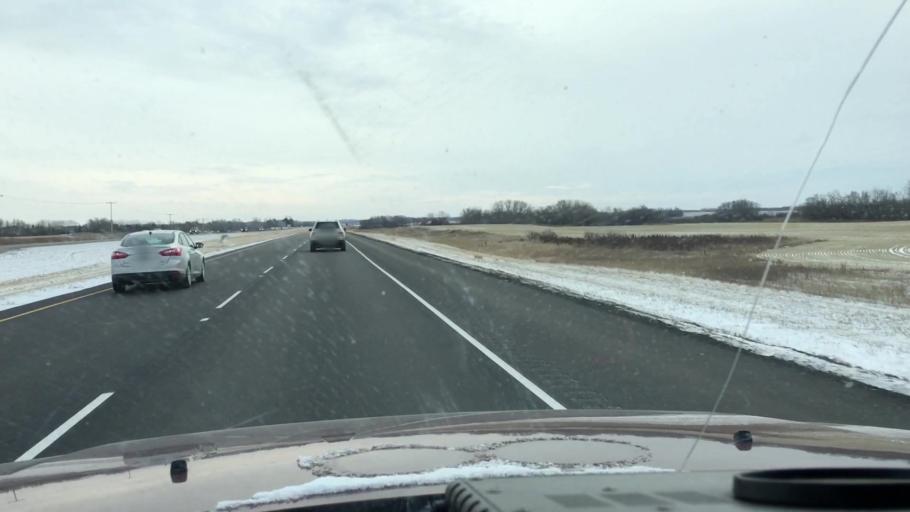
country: CA
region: Saskatchewan
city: Saskatoon
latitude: 52.0259
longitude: -106.5813
